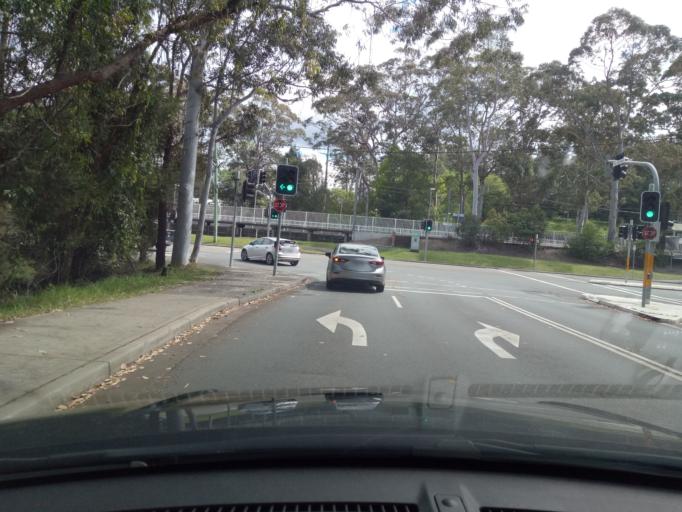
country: AU
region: New South Wales
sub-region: Gosford Shire
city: Lisarow
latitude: -33.3828
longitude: 151.3700
